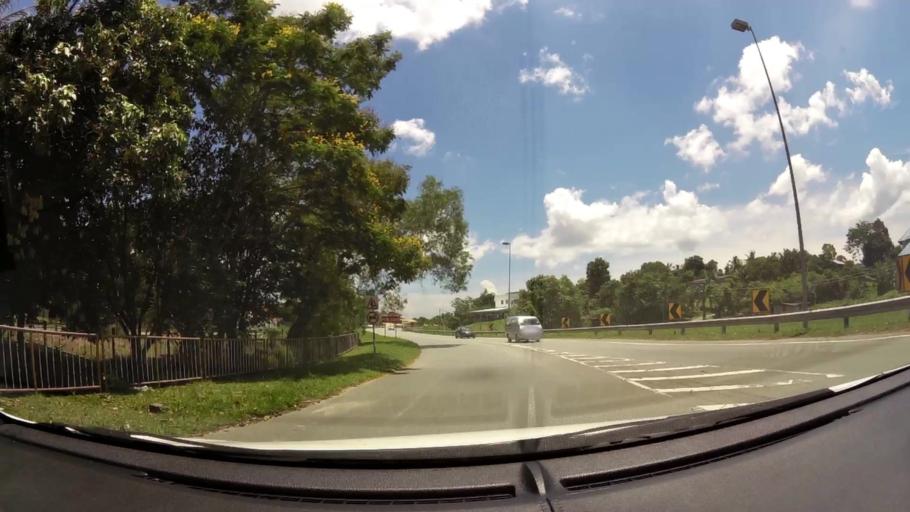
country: BN
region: Brunei and Muara
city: Bandar Seri Begawan
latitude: 4.9345
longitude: 114.9582
